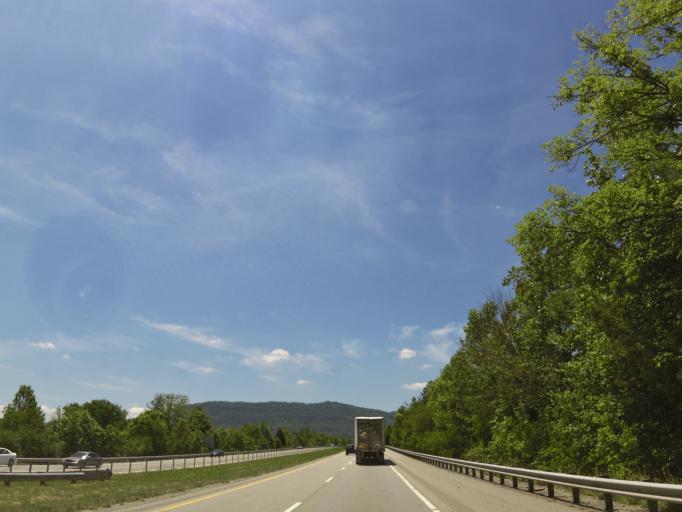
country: US
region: Tennessee
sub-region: Campbell County
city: Jellico
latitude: 36.6096
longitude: -84.1061
